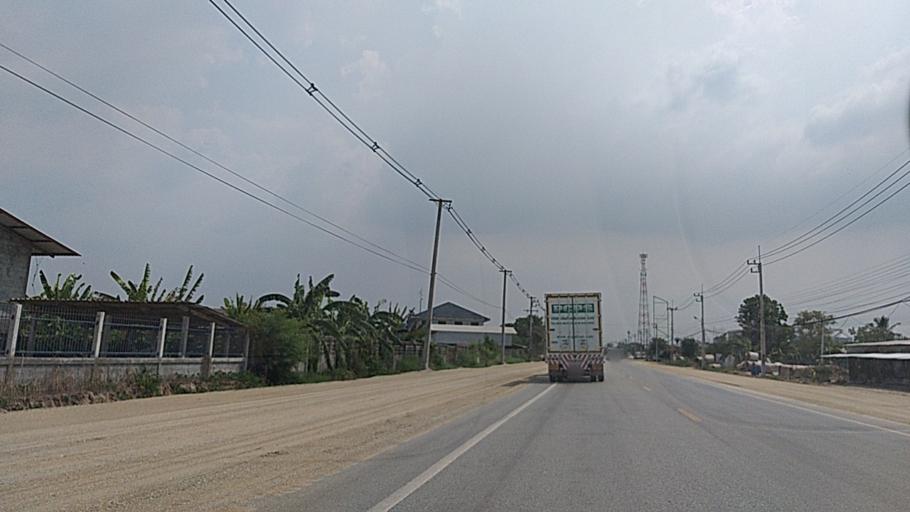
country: TH
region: Chon Buri
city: Phanat Nikhom
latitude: 13.3558
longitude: 101.1961
